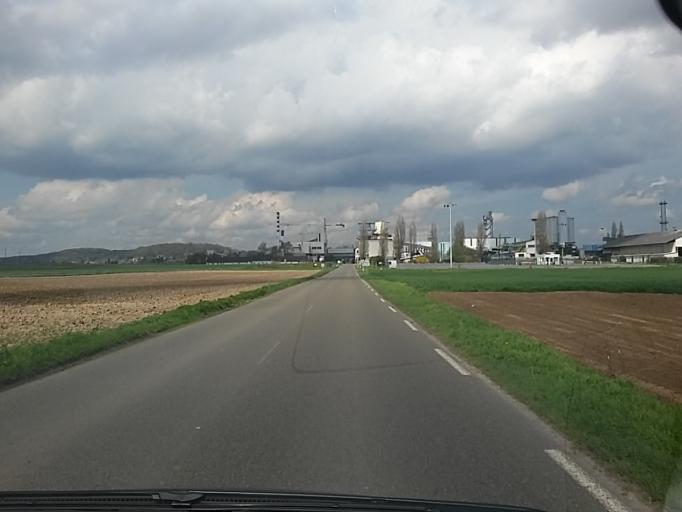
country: FR
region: Picardie
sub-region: Departement de l'Oise
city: Chevrieres
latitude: 49.3560
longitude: 2.6705
